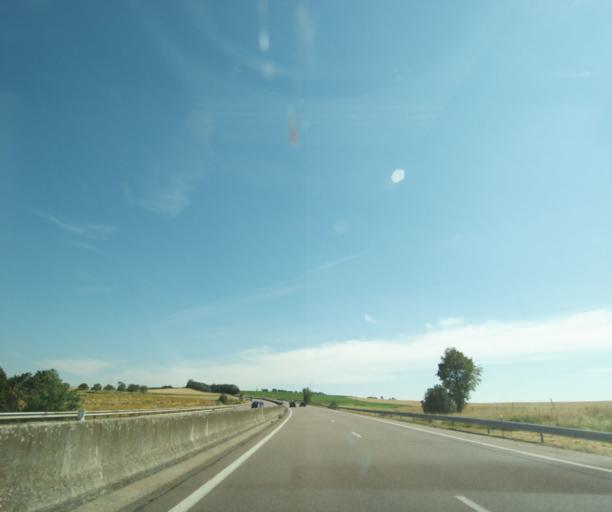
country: FR
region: Lorraine
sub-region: Departement des Vosges
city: Chatenois
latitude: 48.3733
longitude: 5.8777
